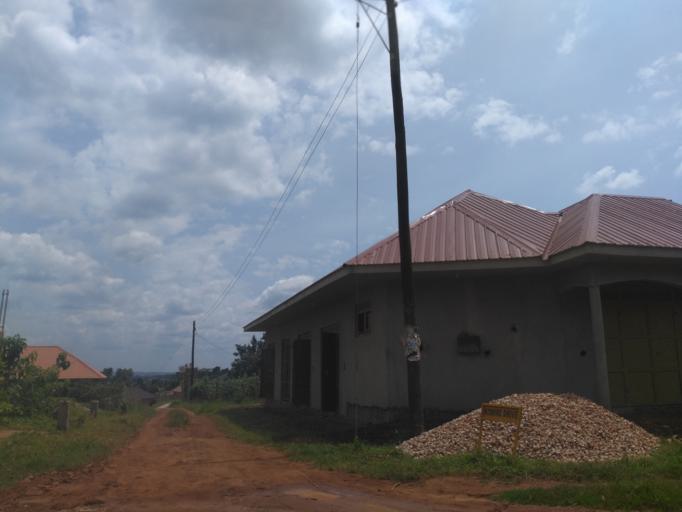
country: UG
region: Central Region
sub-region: Wakiso District
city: Bweyogerere
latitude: 0.4692
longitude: 32.6303
